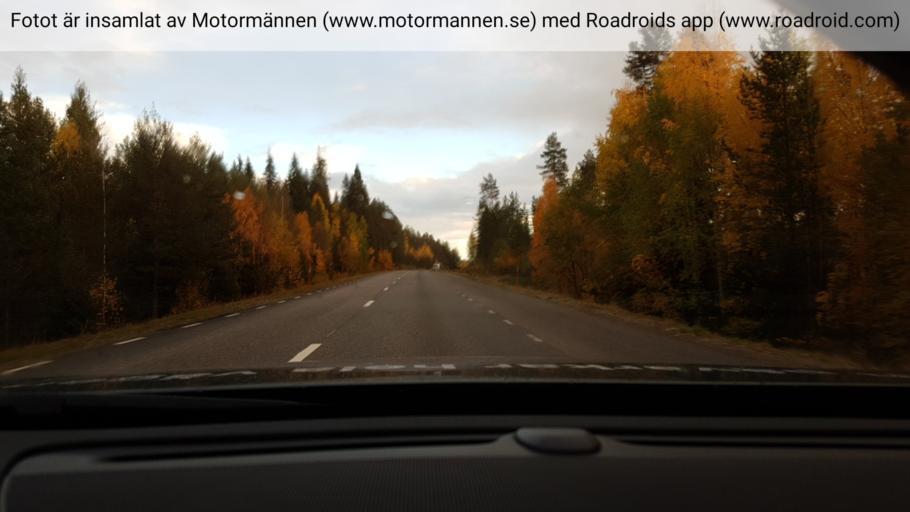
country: SE
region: Norrbotten
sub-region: Overkalix Kommun
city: OEverkalix
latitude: 66.5221
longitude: 22.7626
